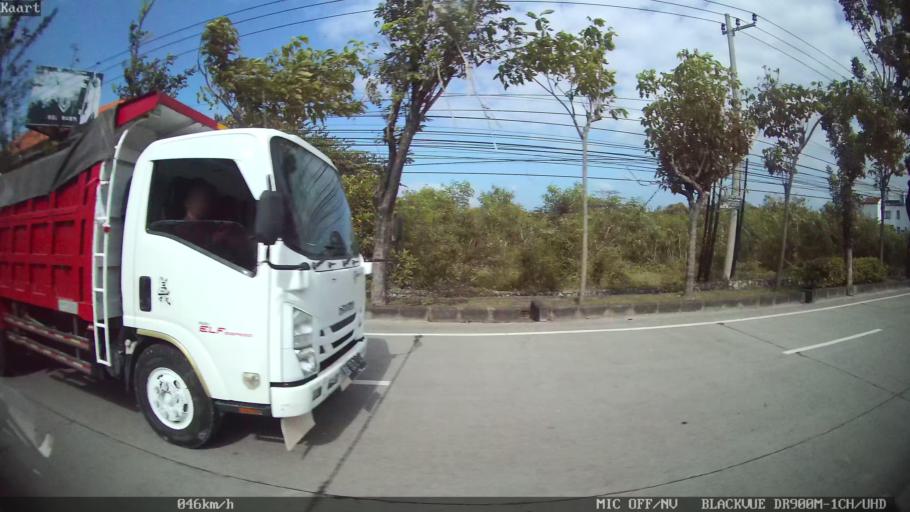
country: ID
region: Bali
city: Kuta
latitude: -8.6958
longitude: 115.1757
